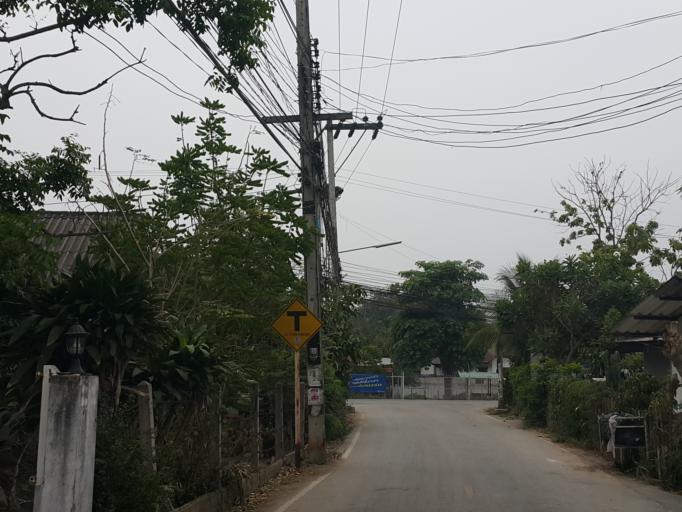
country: TH
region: Chiang Mai
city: Saraphi
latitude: 18.7230
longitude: 99.0026
